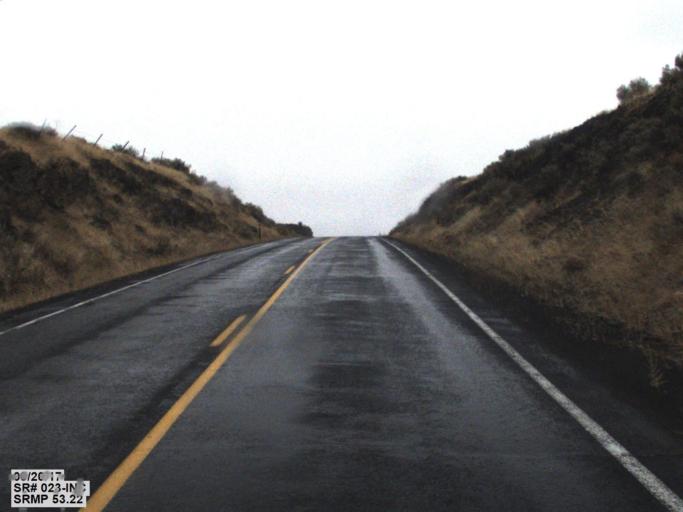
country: US
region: Washington
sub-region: Lincoln County
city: Davenport
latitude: 47.3654
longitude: -118.1117
